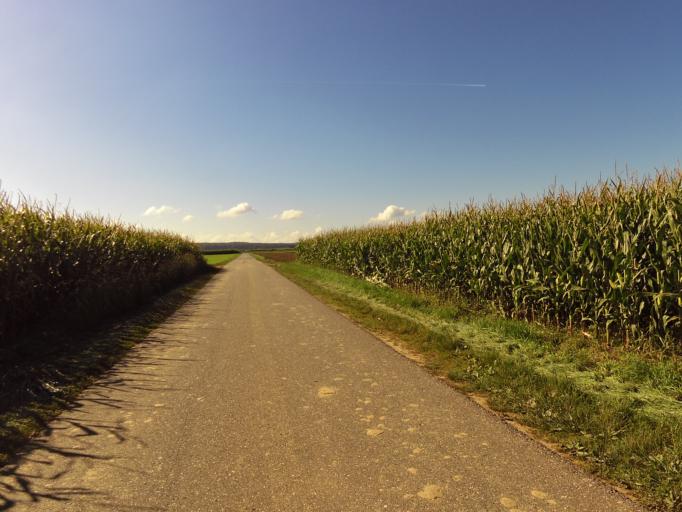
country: DE
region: North Rhine-Westphalia
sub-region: Regierungsbezirk Koln
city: Rheinbach
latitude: 50.6439
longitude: 6.9126
